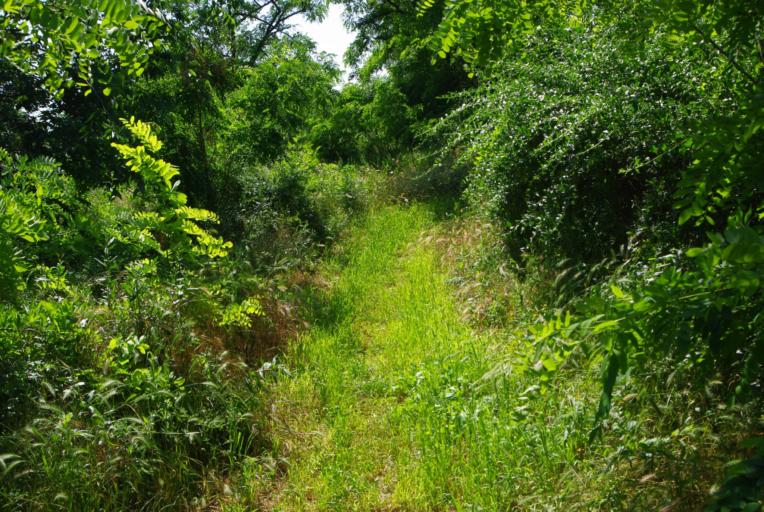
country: HU
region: Tolna
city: Dunafoldvar
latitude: 46.8064
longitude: 18.9329
